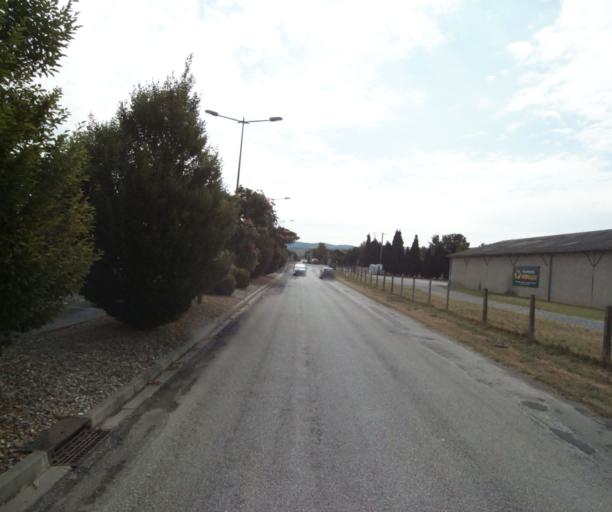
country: FR
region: Midi-Pyrenees
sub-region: Departement de la Haute-Garonne
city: Revel
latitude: 43.4575
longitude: 1.9926
